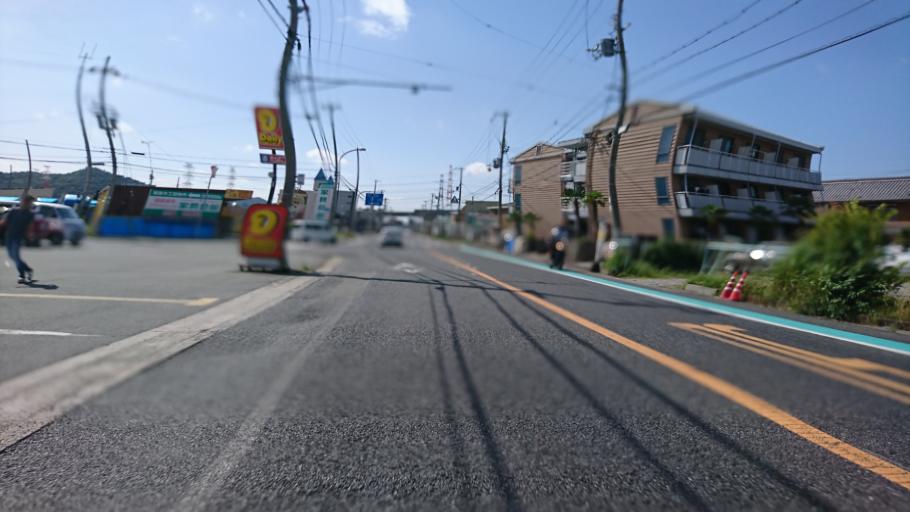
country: JP
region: Hyogo
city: Shirahamacho-usazakiminami
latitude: 34.8156
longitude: 134.7442
